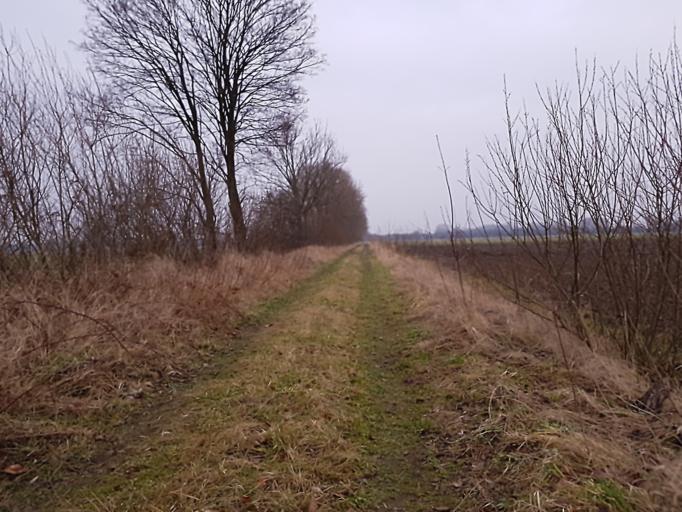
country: BE
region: Flanders
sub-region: Provincie Antwerpen
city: Stabroek
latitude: 51.3365
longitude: 4.3374
